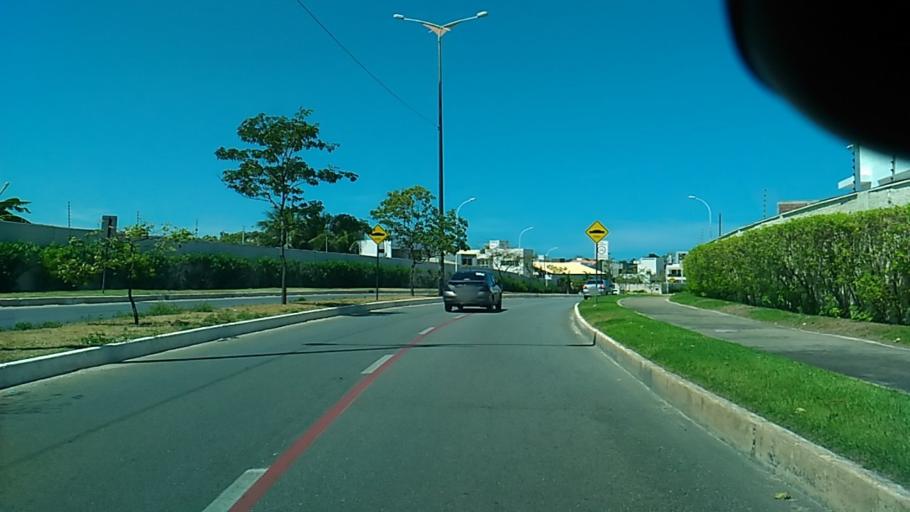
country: BR
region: Paraiba
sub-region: Joao Pessoa
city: Joao Pessoa
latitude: -7.1562
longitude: -34.8190
